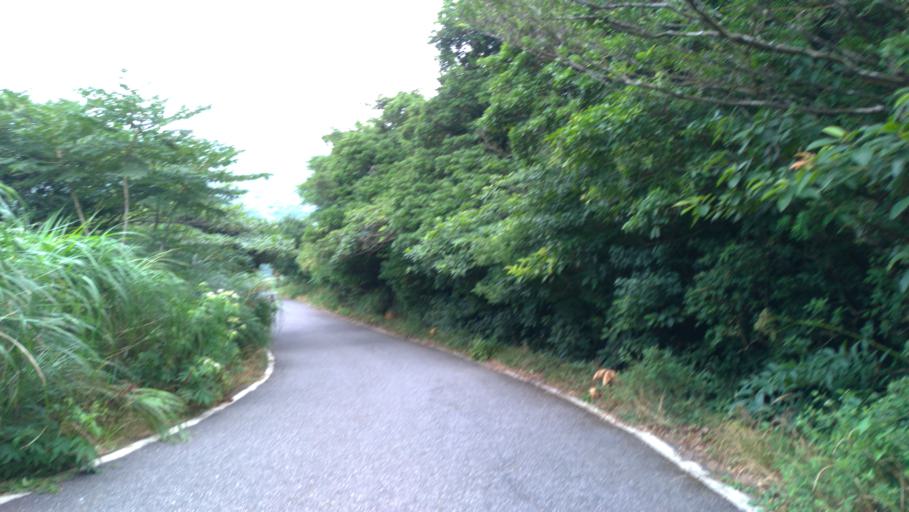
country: TW
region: Taipei
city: Taipei
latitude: 25.1824
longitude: 121.5247
